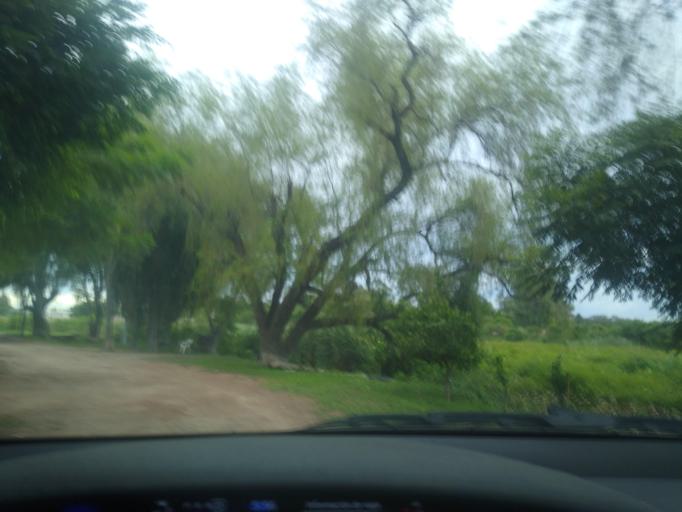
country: AR
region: Chaco
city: Barranqueras
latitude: -27.4646
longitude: -58.9453
